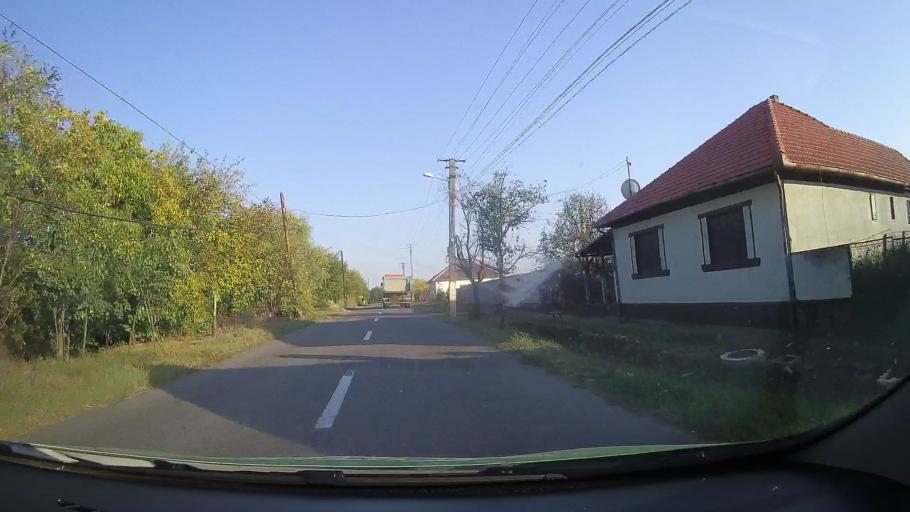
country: RO
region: Arad
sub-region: Comuna Pancota
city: Pancota
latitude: 46.3172
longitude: 21.6980
